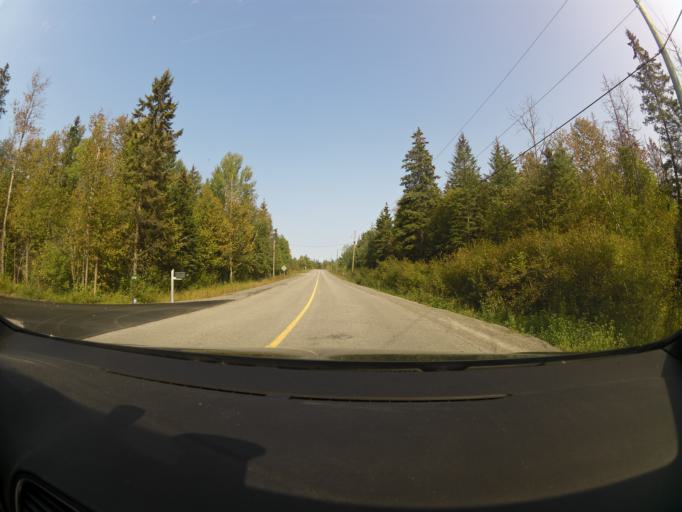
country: CA
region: Ontario
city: Carleton Place
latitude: 45.3290
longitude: -76.1655
